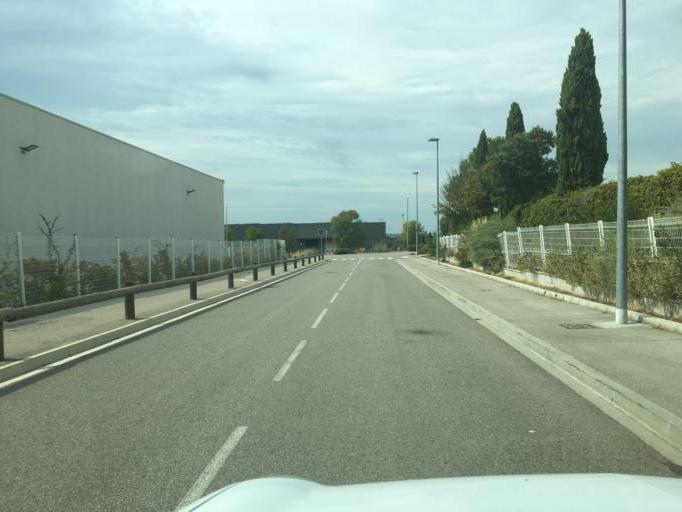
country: FR
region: Provence-Alpes-Cote d'Azur
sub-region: Departement des Bouches-du-Rhone
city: Bouc-Bel-Air
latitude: 43.4838
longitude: 5.3891
